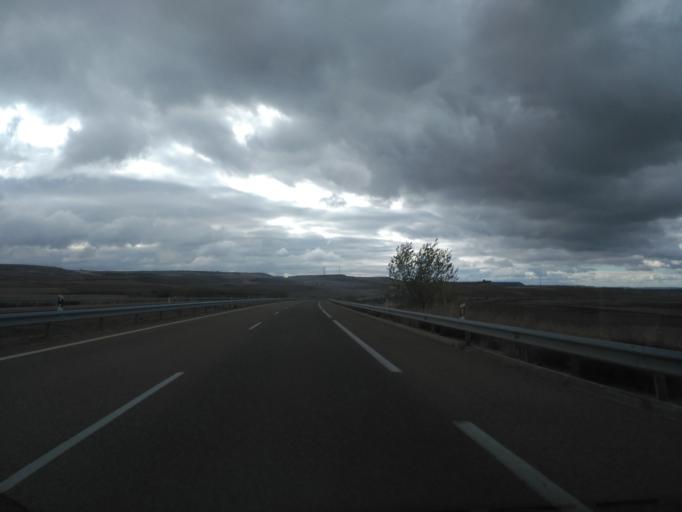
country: ES
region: Castille and Leon
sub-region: Provincia de Palencia
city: Monzon de Campos
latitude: 42.1397
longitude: -4.4700
